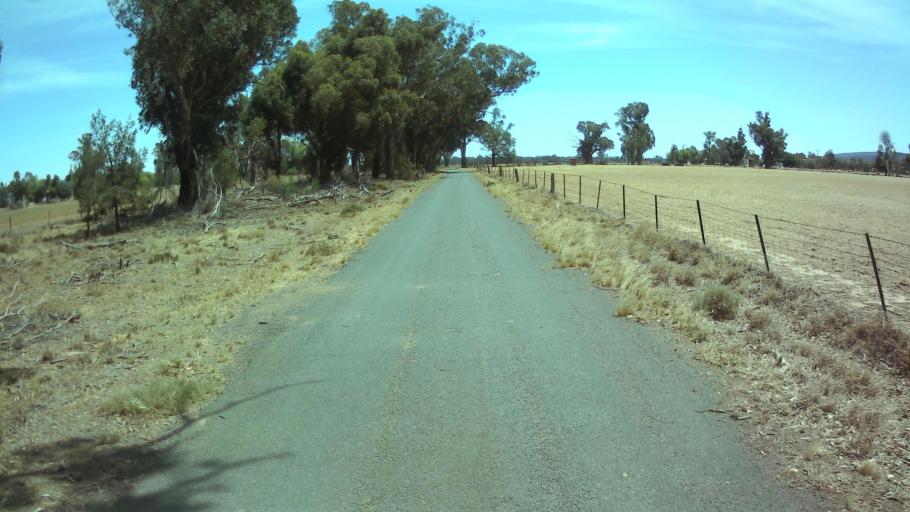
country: AU
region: New South Wales
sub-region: Weddin
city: Grenfell
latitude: -34.0305
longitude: 147.9417
